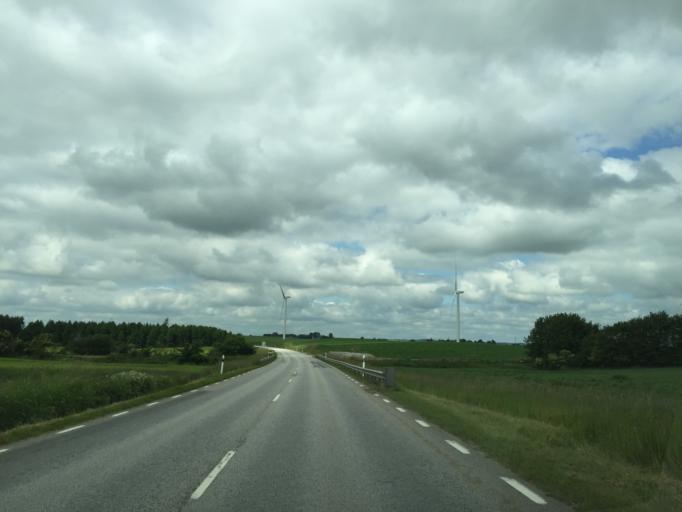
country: SE
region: Skane
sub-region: Svedala Kommun
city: Klagerup
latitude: 55.6038
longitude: 13.2655
